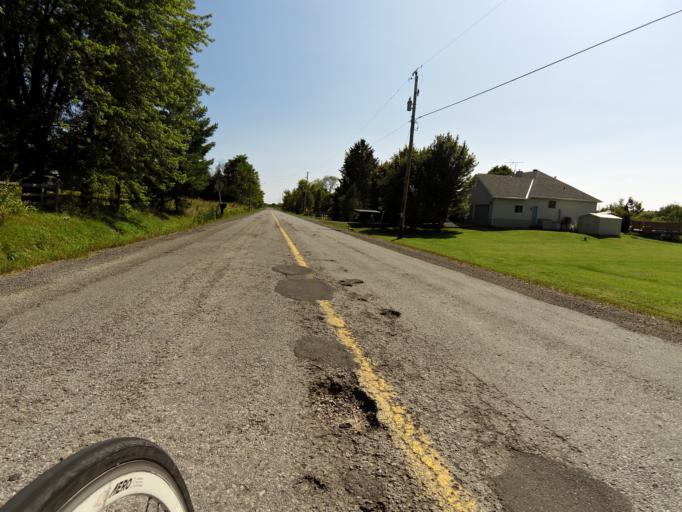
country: CA
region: Ontario
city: Arnprior
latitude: 45.4530
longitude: -76.0876
